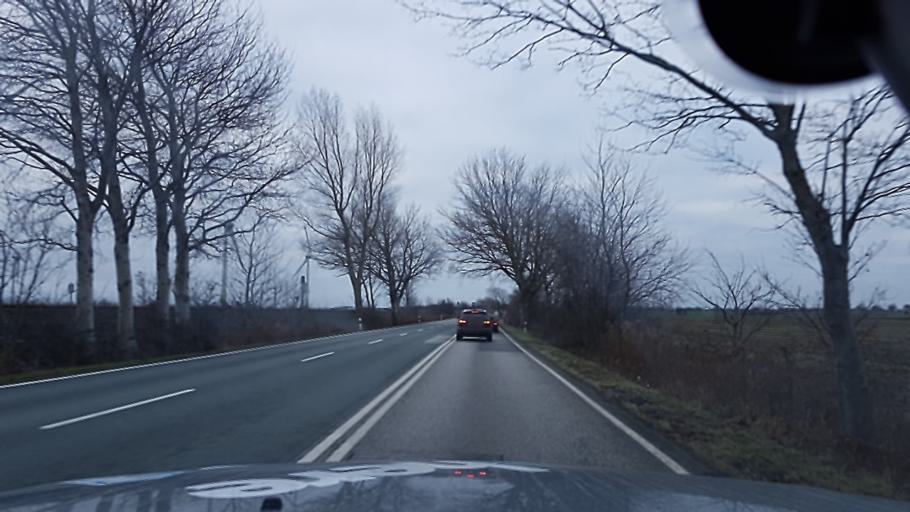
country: DE
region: Schleswig-Holstein
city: Fehmarn
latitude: 54.4886
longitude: 11.2176
